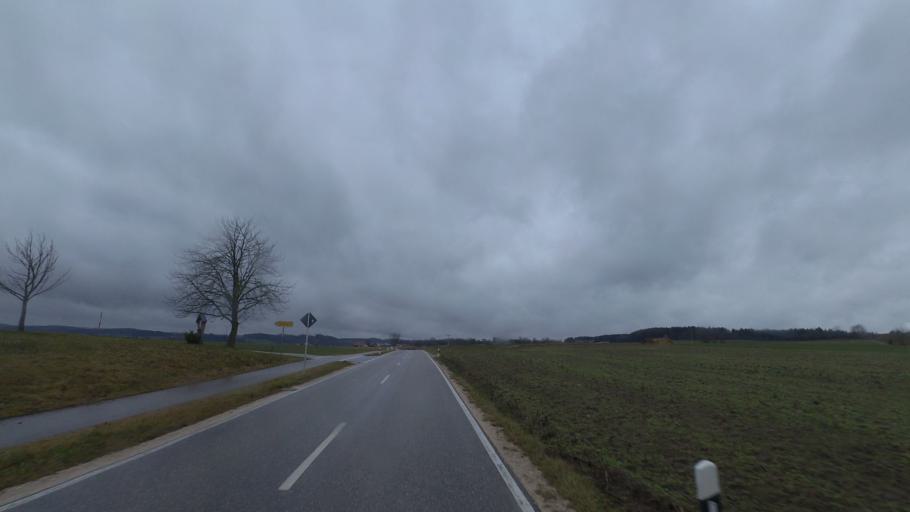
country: DE
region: Bavaria
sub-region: Upper Bavaria
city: Taching am See
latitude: 47.9559
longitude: 12.7755
